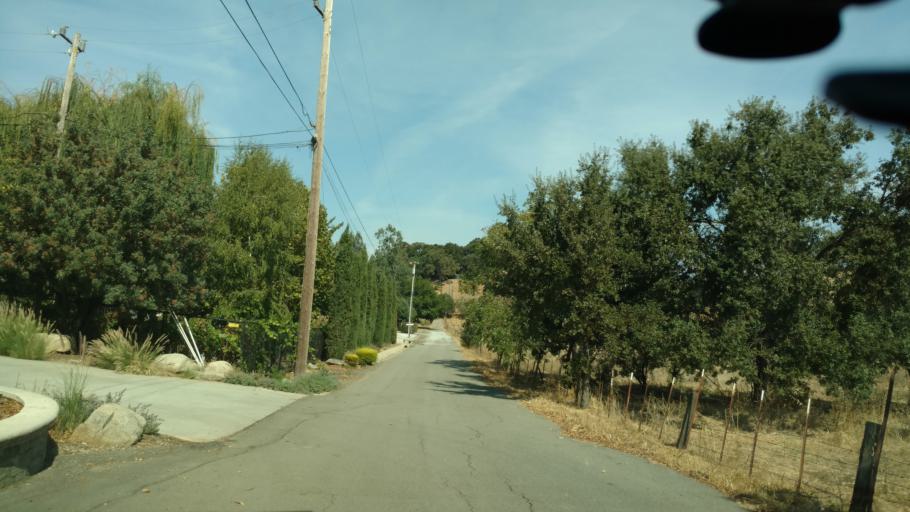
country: US
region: California
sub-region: Santa Clara County
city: Morgan Hill
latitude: 37.1075
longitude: -121.6581
